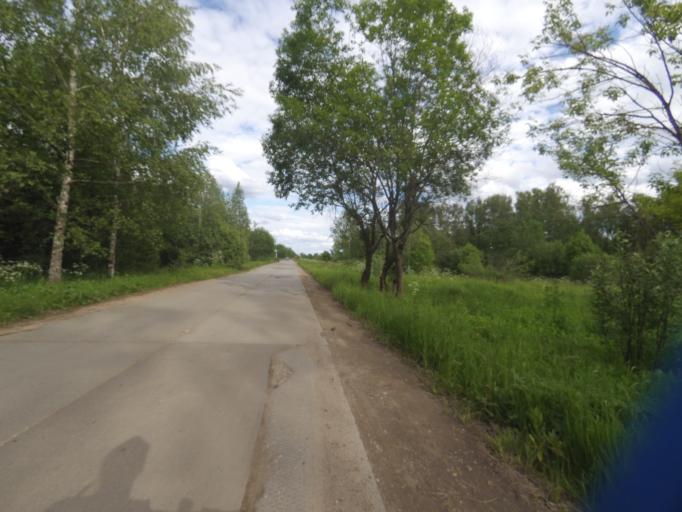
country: RU
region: Moskovskaya
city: Marfino
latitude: 56.1069
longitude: 37.5698
